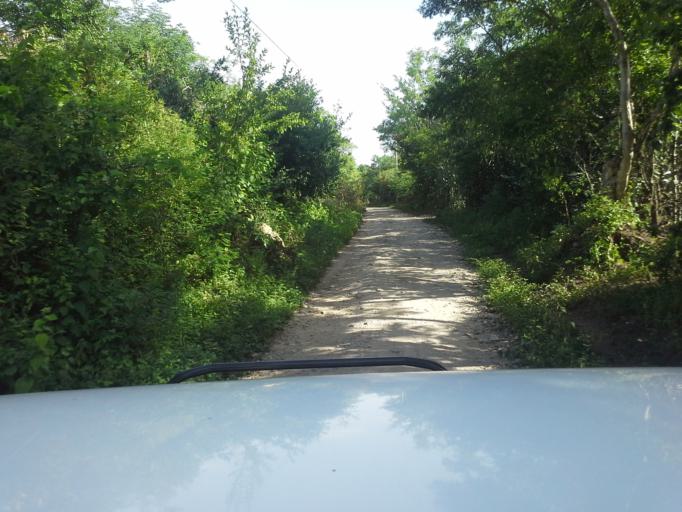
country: NI
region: Matagalpa
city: Ciudad Dario
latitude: 12.6698
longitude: -86.0540
